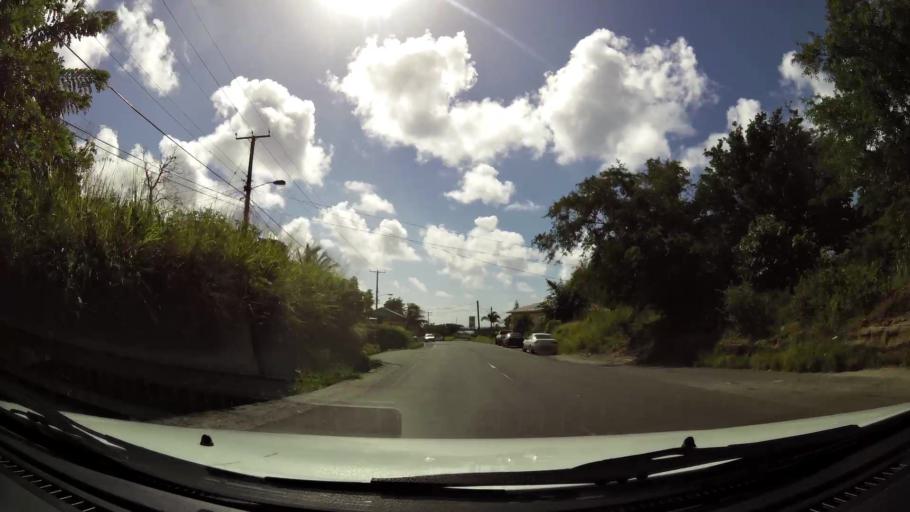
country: LC
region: Choiseul Quarter
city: Choiseul
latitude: 13.7590
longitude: -61.0230
